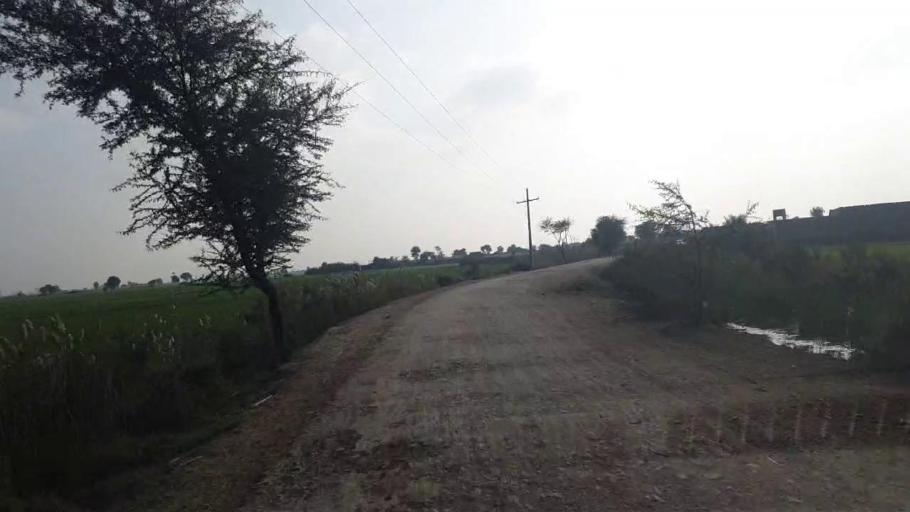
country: PK
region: Sindh
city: Shahdadpur
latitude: 25.8773
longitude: 68.6661
